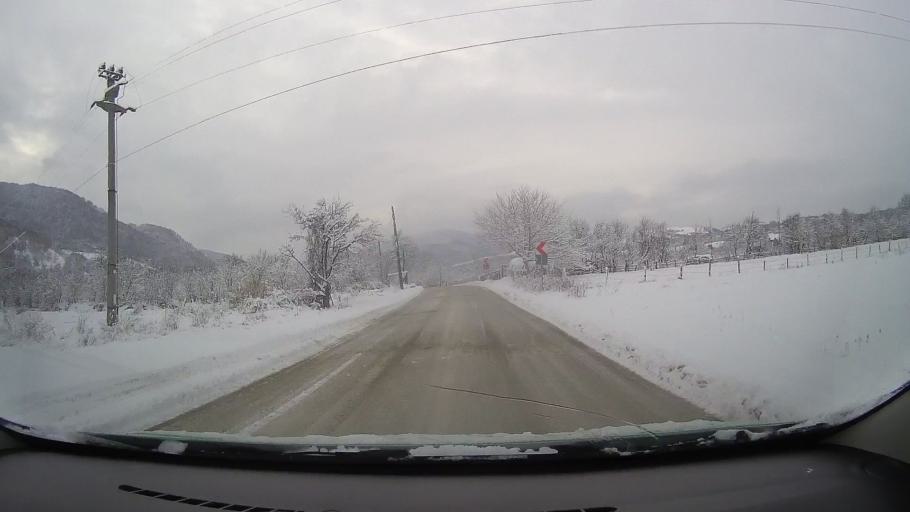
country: RO
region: Alba
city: Pianu de Sus
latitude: 45.9086
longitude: 23.4802
